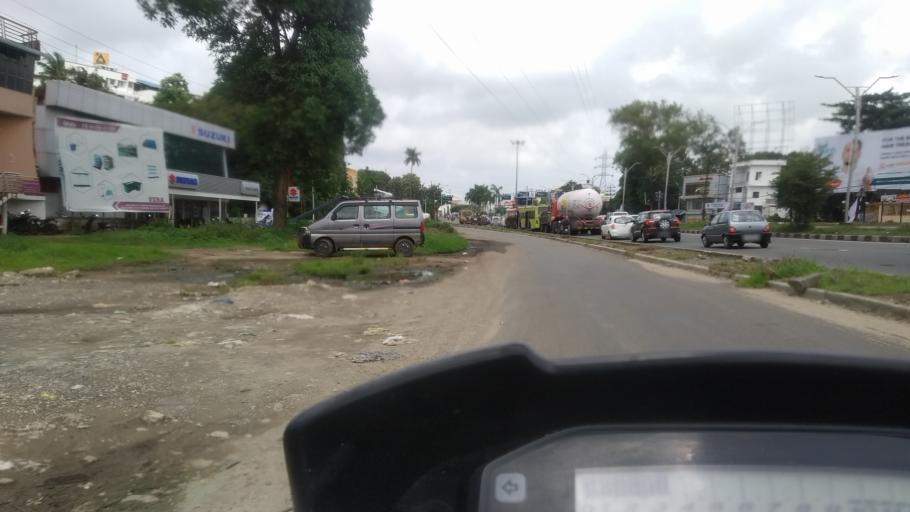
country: IN
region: Kerala
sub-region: Ernakulam
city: Aluva
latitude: 10.1152
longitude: 76.3455
